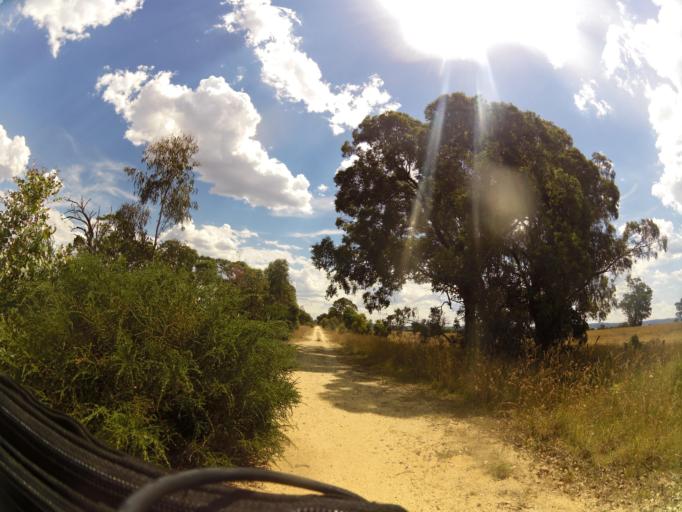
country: AU
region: Victoria
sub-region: Wellington
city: Heyfield
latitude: -37.9804
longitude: 146.7404
